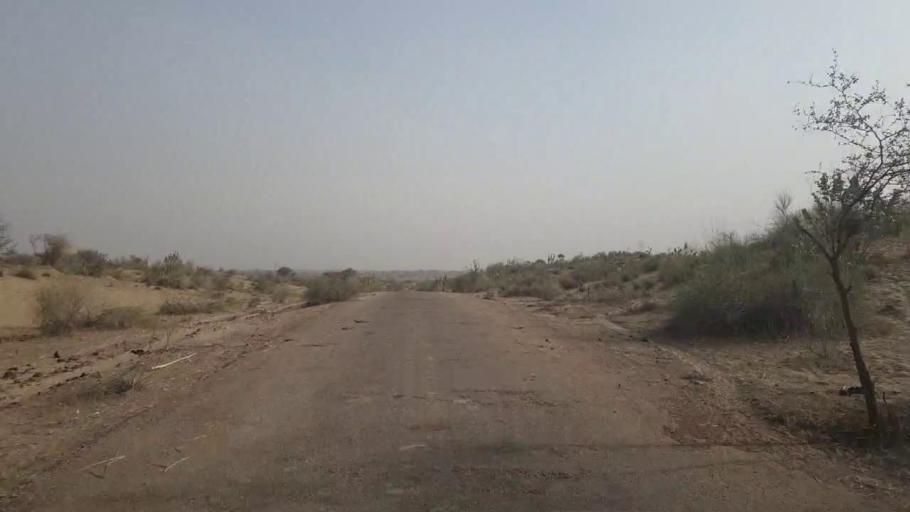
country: PK
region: Sindh
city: Chor
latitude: 25.5089
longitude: 69.9681
